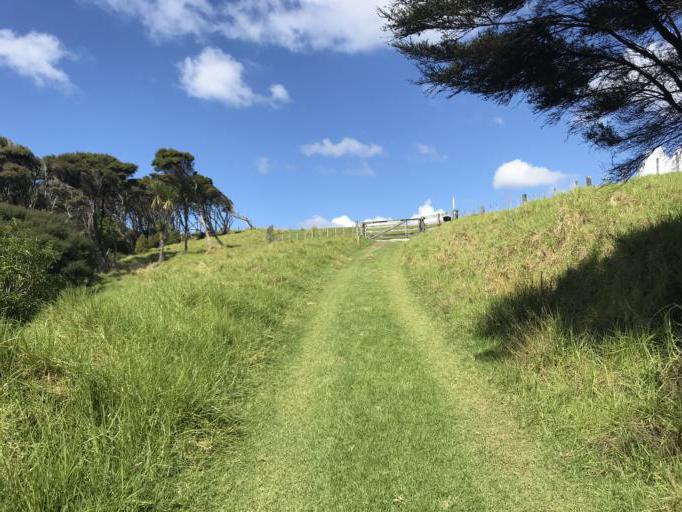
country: NZ
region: Auckland
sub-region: Auckland
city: Warkworth
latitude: -36.3742
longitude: 174.8440
